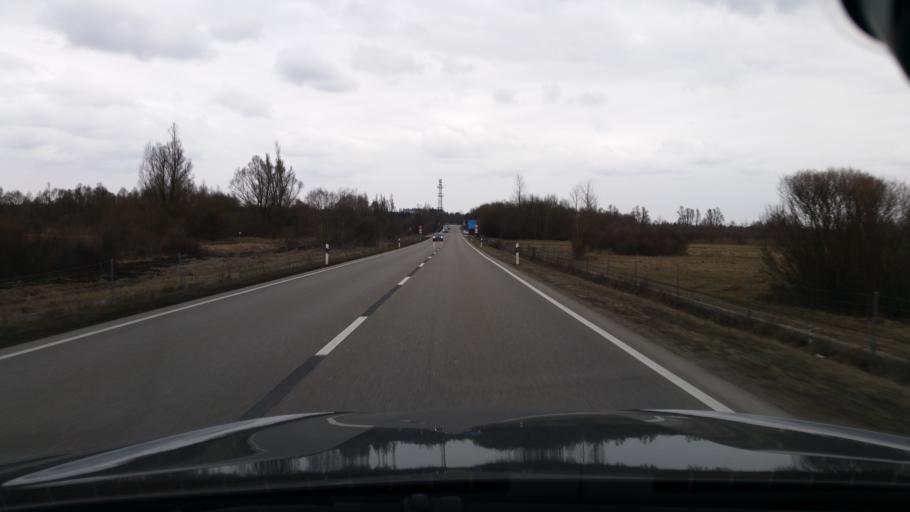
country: DE
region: Bavaria
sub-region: Upper Bavaria
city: Langenbach
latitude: 48.3915
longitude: 11.8590
